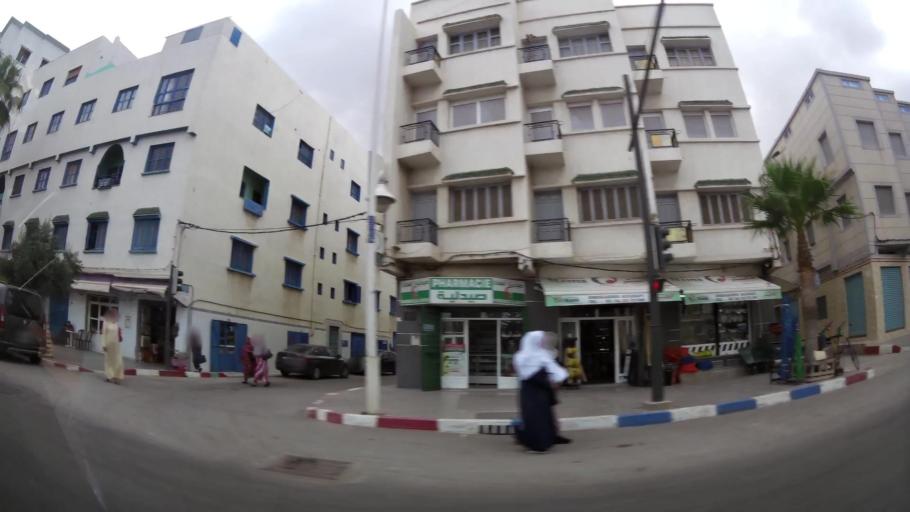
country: MA
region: Oriental
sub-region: Nador
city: Nador
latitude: 35.1564
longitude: -2.9297
